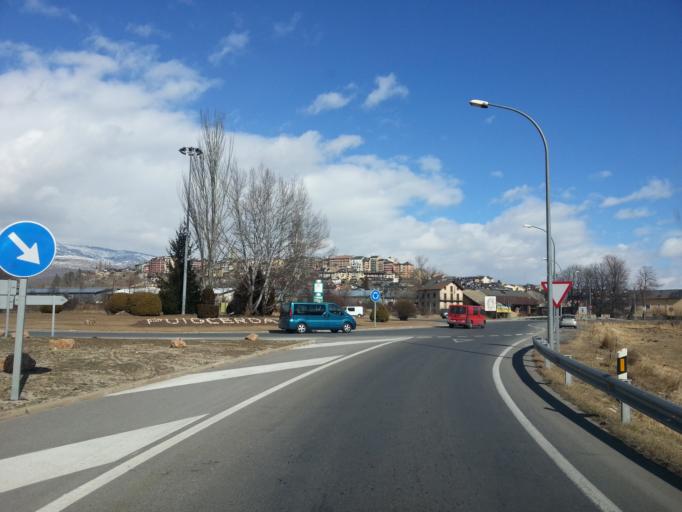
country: ES
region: Catalonia
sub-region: Provincia de Girona
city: Puigcerda
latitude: 42.4250
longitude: 1.9233
